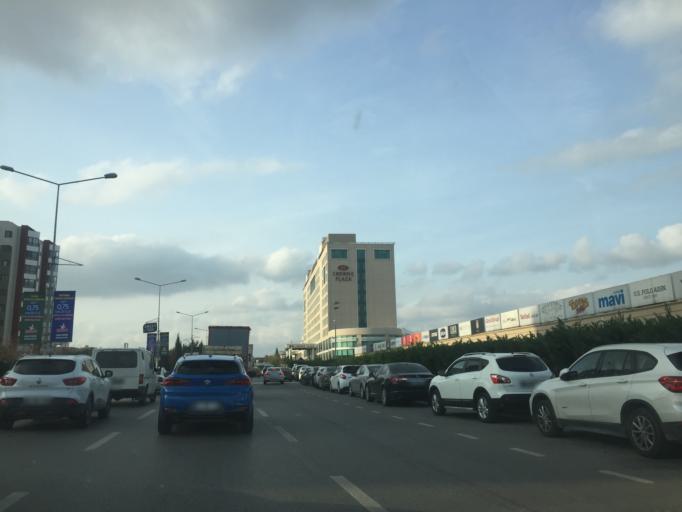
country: TR
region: Istanbul
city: Sultanbeyli
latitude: 40.9369
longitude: 29.3247
